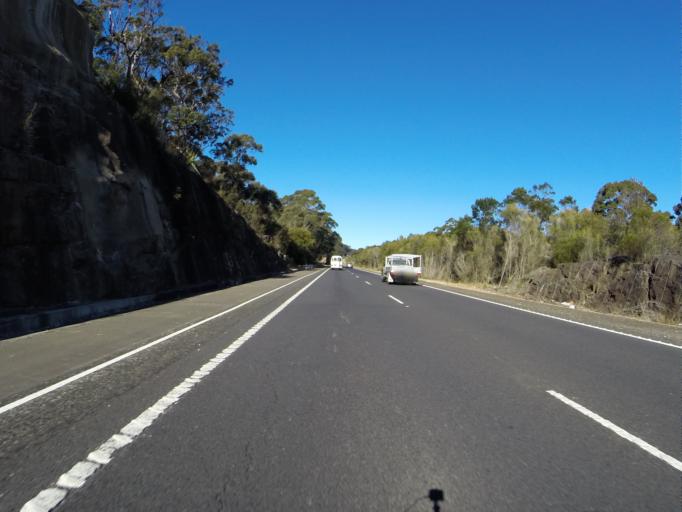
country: AU
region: New South Wales
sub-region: Wollongong
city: Helensburgh
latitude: -34.1946
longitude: 150.9665
